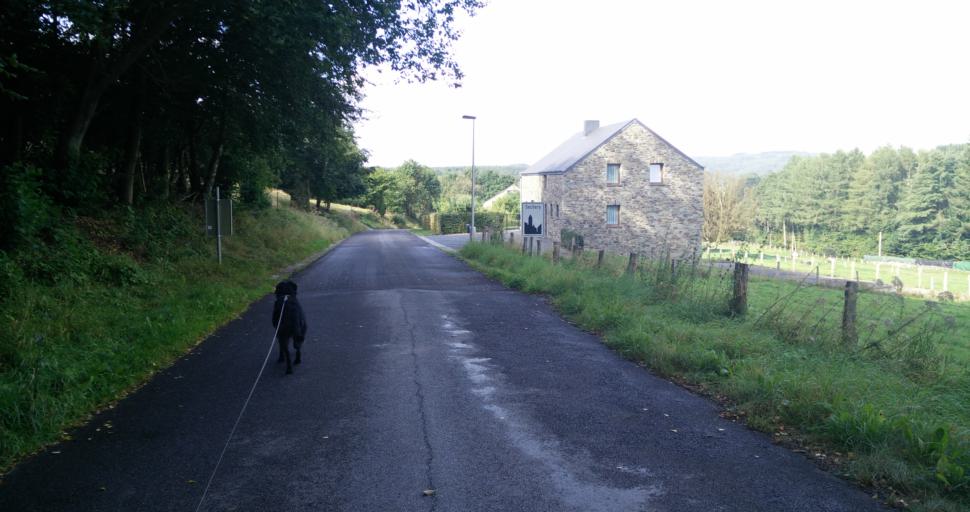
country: BE
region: Wallonia
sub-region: Province du Luxembourg
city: Daverdisse
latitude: 50.0118
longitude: 5.1530
